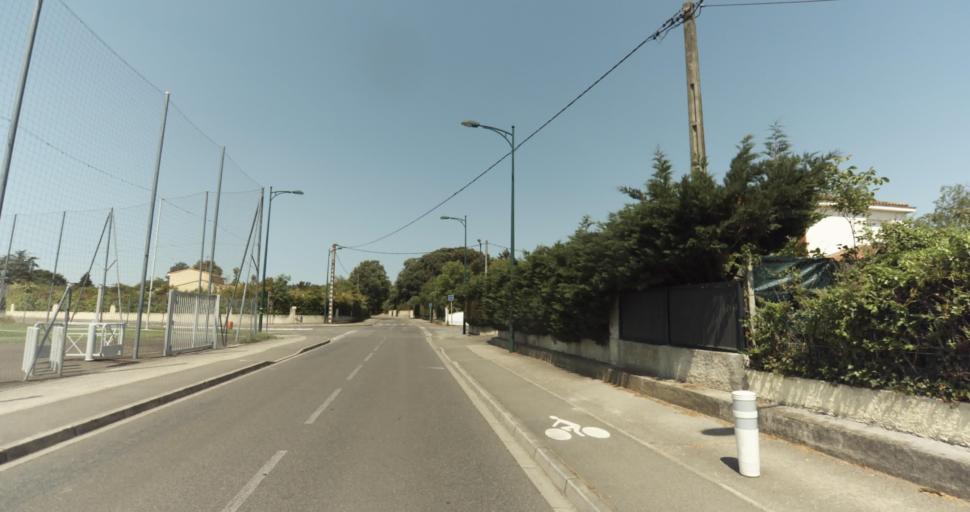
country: FR
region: Midi-Pyrenees
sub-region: Departement de la Haute-Garonne
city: Plaisance-du-Touch
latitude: 43.5655
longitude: 1.2876
